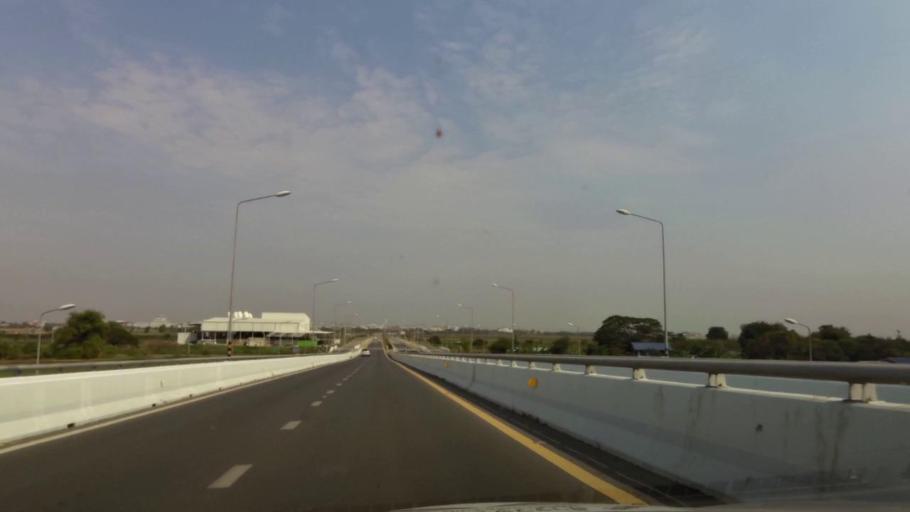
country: TH
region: Phra Nakhon Si Ayutthaya
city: Phra Nakhon Si Ayutthaya
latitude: 14.3312
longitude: 100.5842
